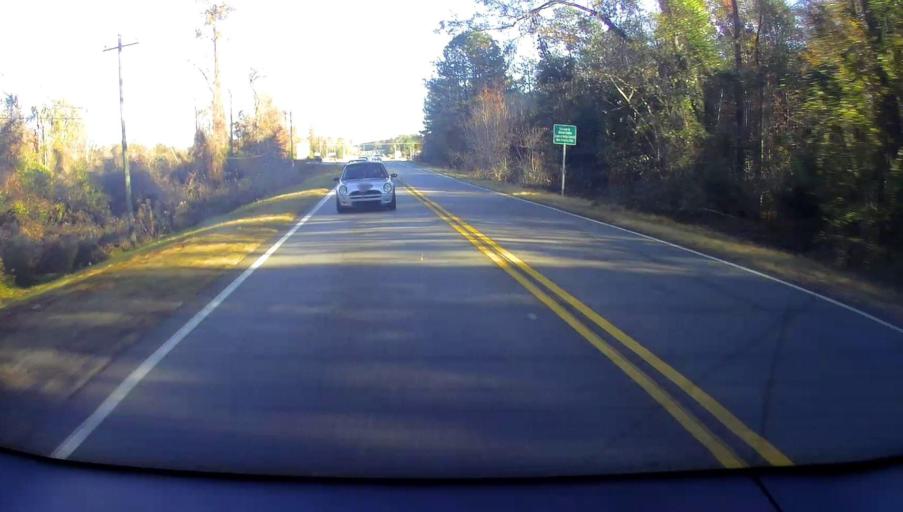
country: US
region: Georgia
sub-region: Houston County
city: Centerville
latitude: 32.6113
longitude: -83.7123
